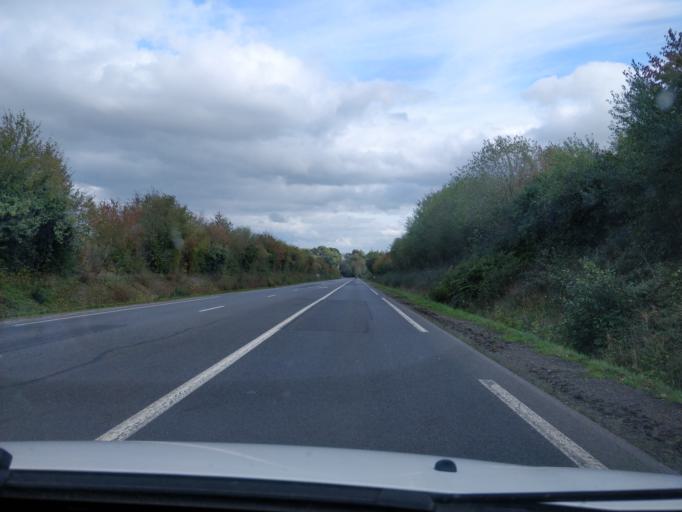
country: FR
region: Lower Normandy
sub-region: Departement du Calvados
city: Saint-Sever-Calvados
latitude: 48.8382
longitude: -1.0231
